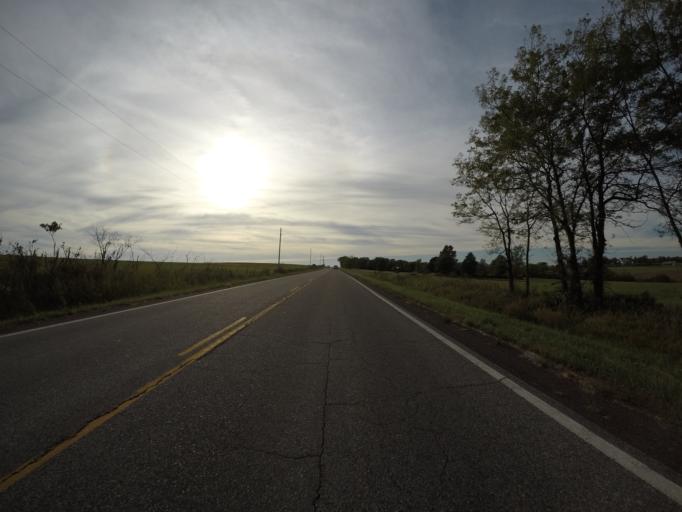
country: US
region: Kansas
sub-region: Douglas County
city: Baldwin City
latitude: 38.7823
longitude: -95.2374
